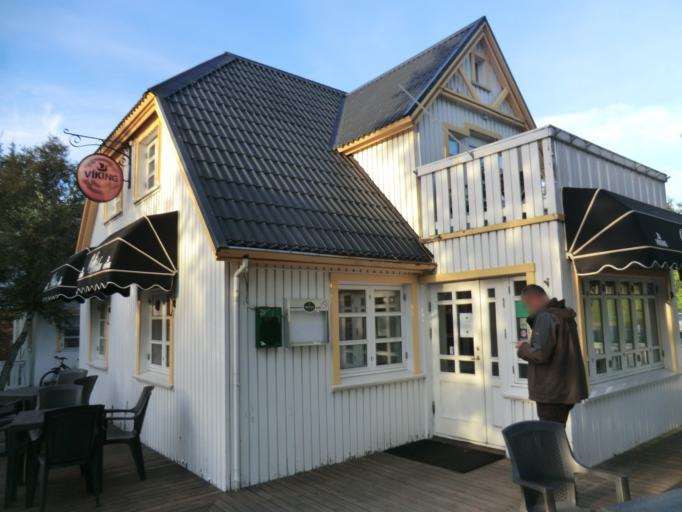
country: IS
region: East
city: Egilsstadir
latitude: 65.2615
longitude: -14.3993
